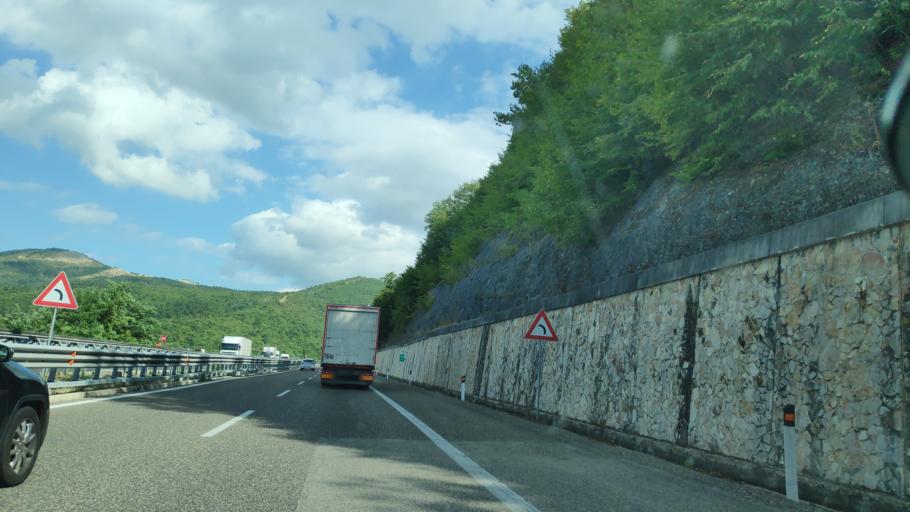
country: IT
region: Campania
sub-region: Provincia di Salerno
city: Pertosa
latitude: 40.5324
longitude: 15.4256
